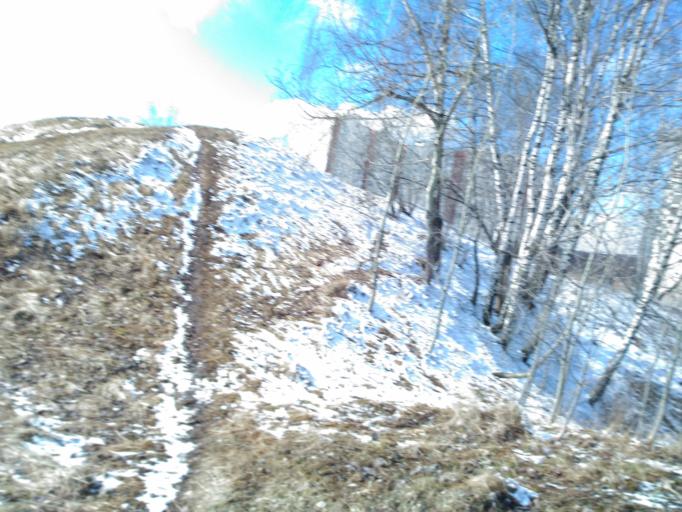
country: RU
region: Moscow
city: Shchukino
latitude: 55.7684
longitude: 37.4152
